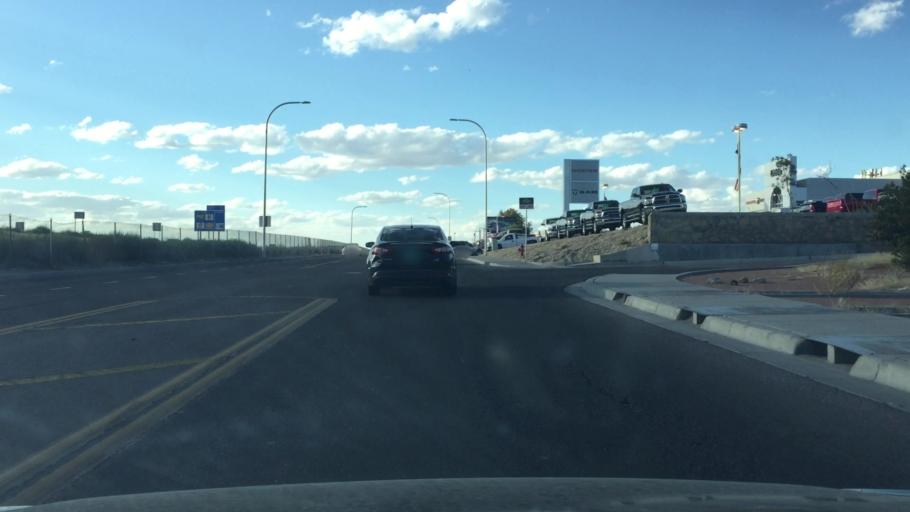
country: US
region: New Mexico
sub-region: Dona Ana County
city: Las Cruces
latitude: 32.3290
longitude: -106.7558
